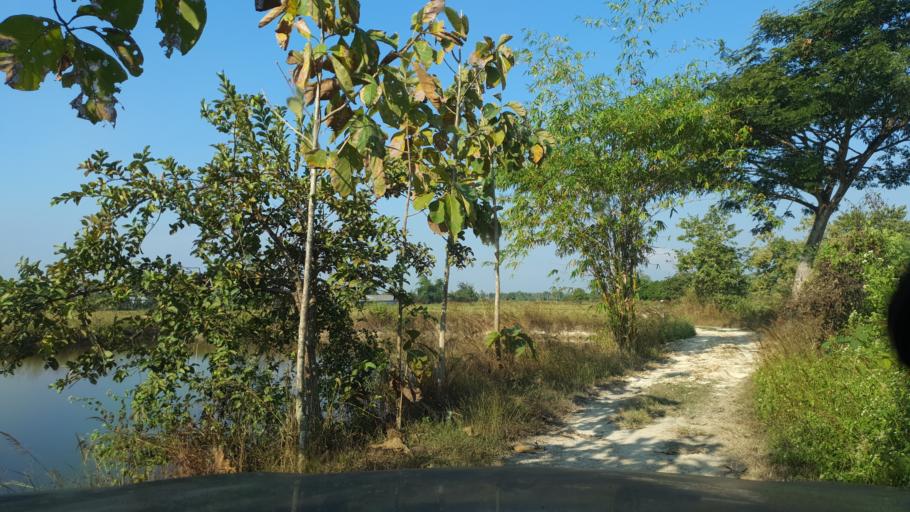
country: TH
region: Lamphun
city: Ban Thi
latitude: 18.6751
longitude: 99.1359
